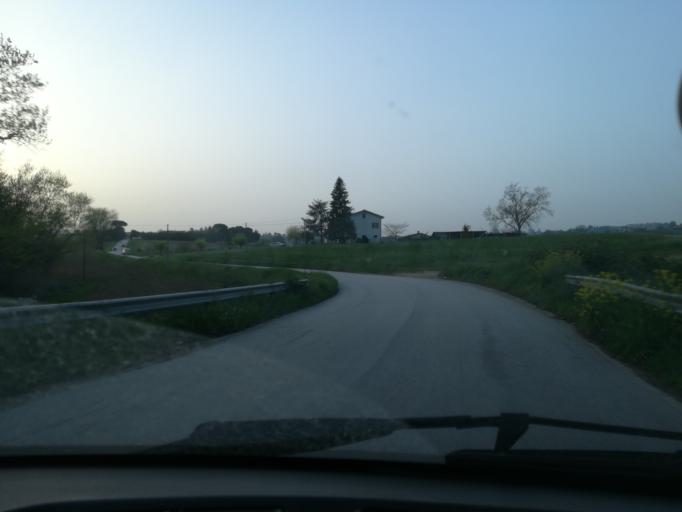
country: IT
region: The Marches
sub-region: Provincia di Macerata
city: Piediripa
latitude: 43.2700
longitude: 13.4617
